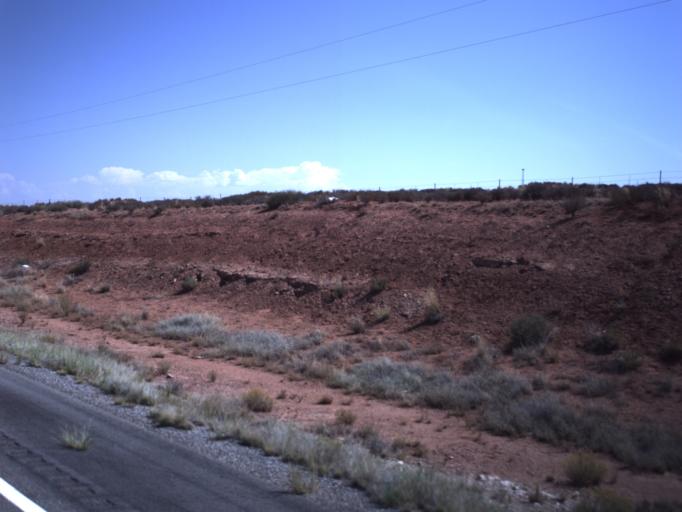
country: US
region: Utah
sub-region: San Juan County
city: Blanding
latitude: 37.0256
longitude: -109.6016
